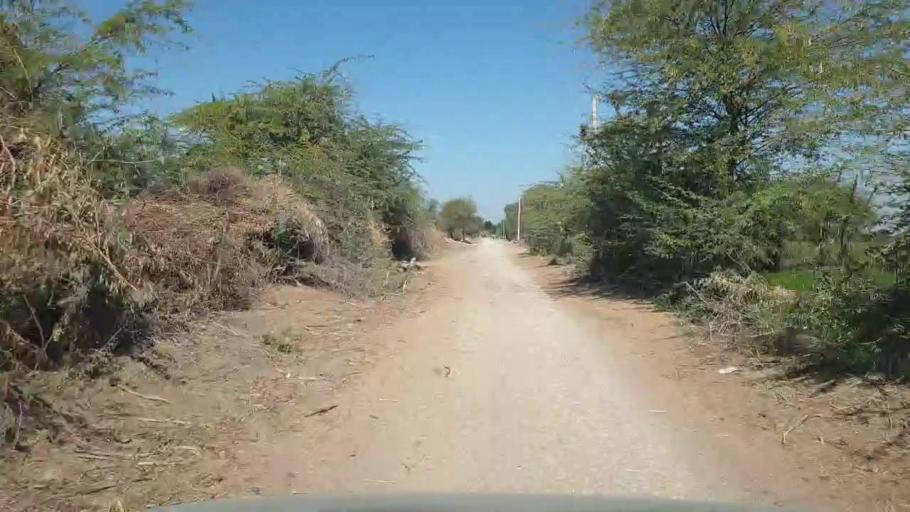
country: PK
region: Sindh
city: Mirwah Gorchani
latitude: 25.3154
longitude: 69.1282
